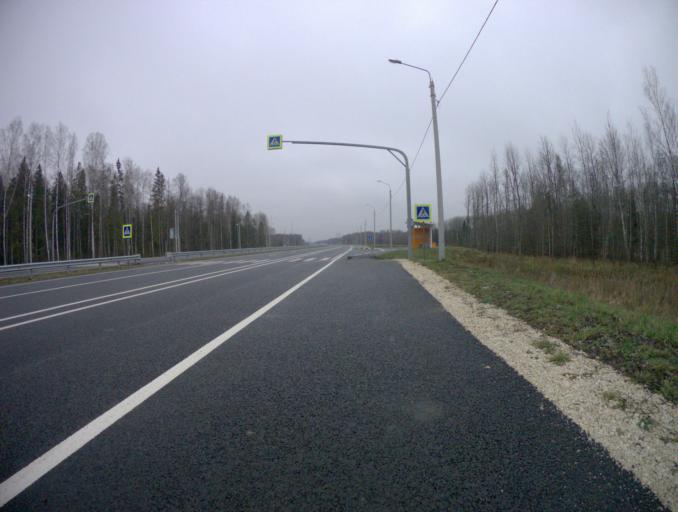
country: RU
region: Vladimir
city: Kommunar
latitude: 56.0419
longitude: 40.5232
